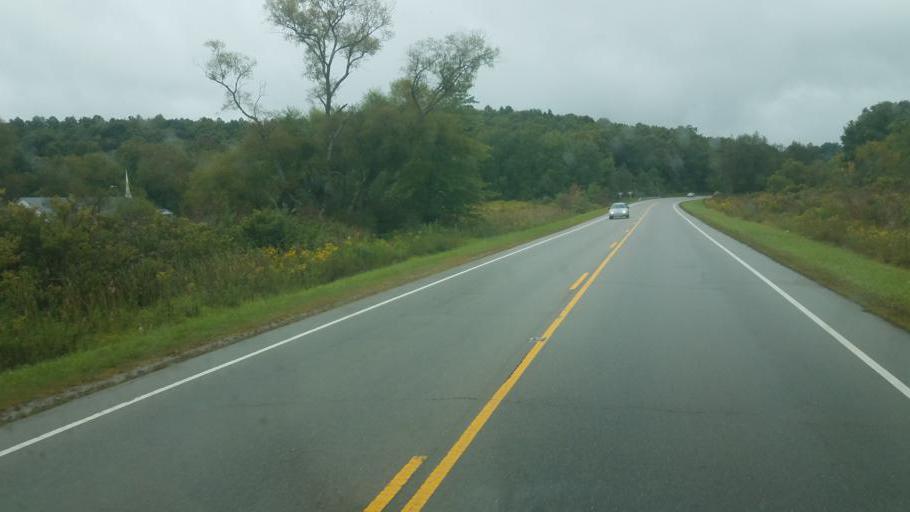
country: US
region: Ohio
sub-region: Jackson County
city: Oak Hill
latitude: 38.8651
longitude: -82.5978
